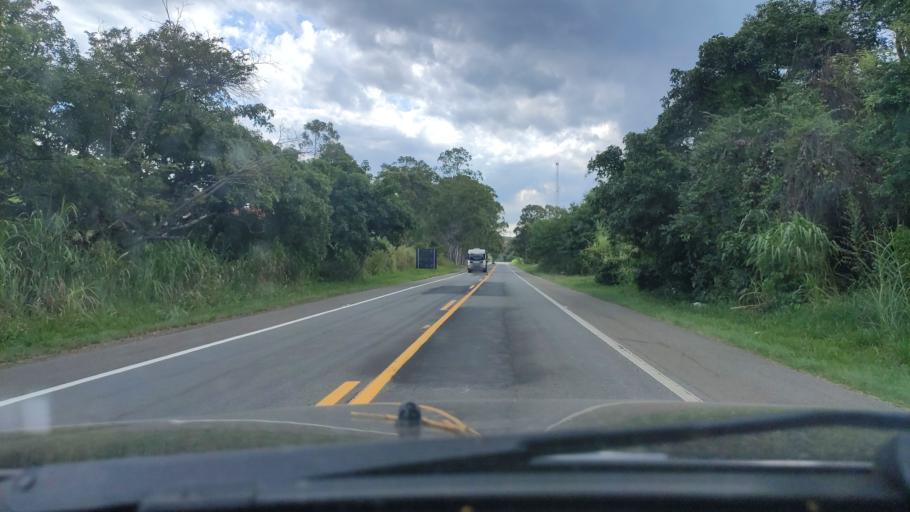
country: BR
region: Sao Paulo
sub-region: Itapira
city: Itapira
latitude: -22.4599
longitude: -46.7344
